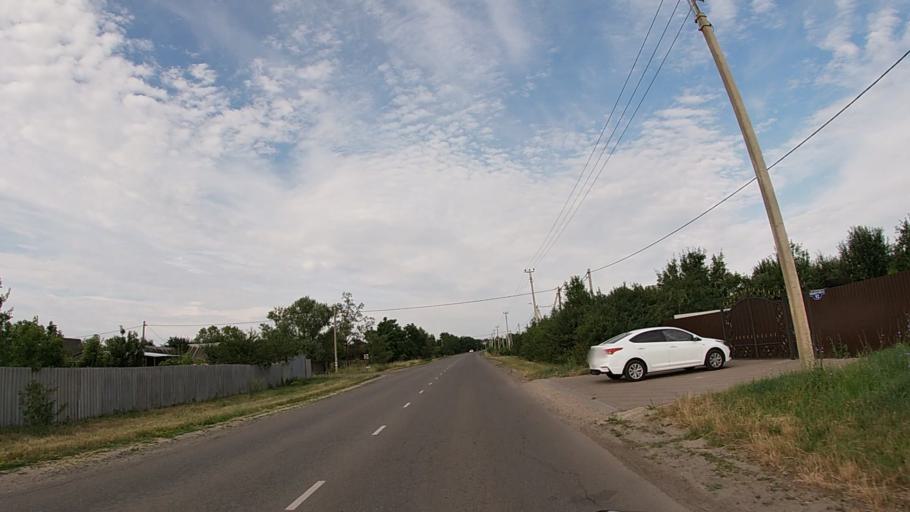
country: RU
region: Belgorod
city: Severnyy
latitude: 50.6968
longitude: 36.5745
